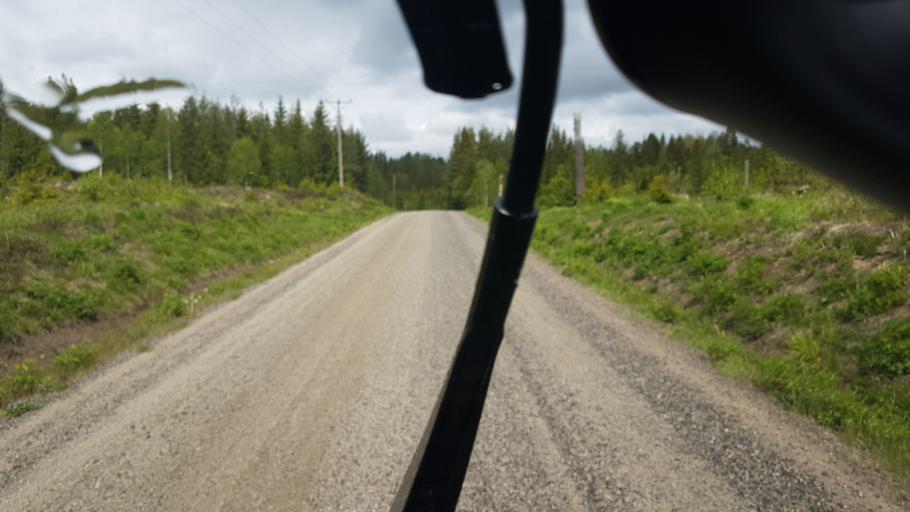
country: SE
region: Vaermland
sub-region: Arvika Kommun
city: Arvika
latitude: 59.8671
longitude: 12.7122
